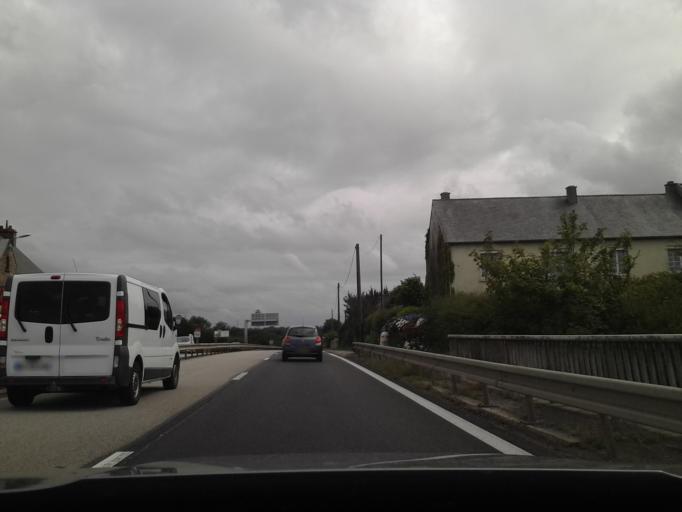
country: FR
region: Lower Normandy
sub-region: Departement de la Manche
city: La Glacerie
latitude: 49.5962
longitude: -1.5964
